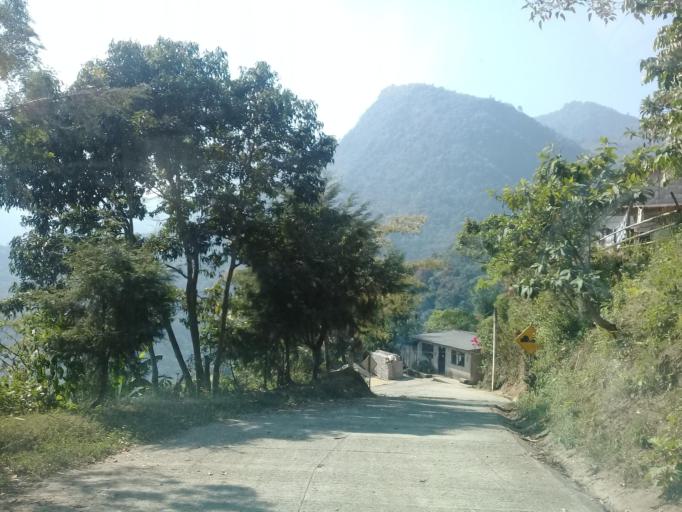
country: MX
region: Veracruz
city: Rafael Delgado
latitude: 18.7835
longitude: -97.0289
